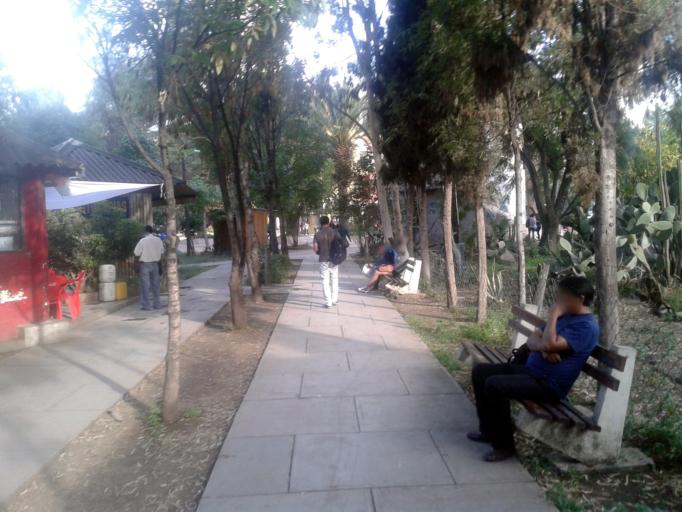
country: BO
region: Cochabamba
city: Cochabamba
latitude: -17.3935
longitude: -66.1485
